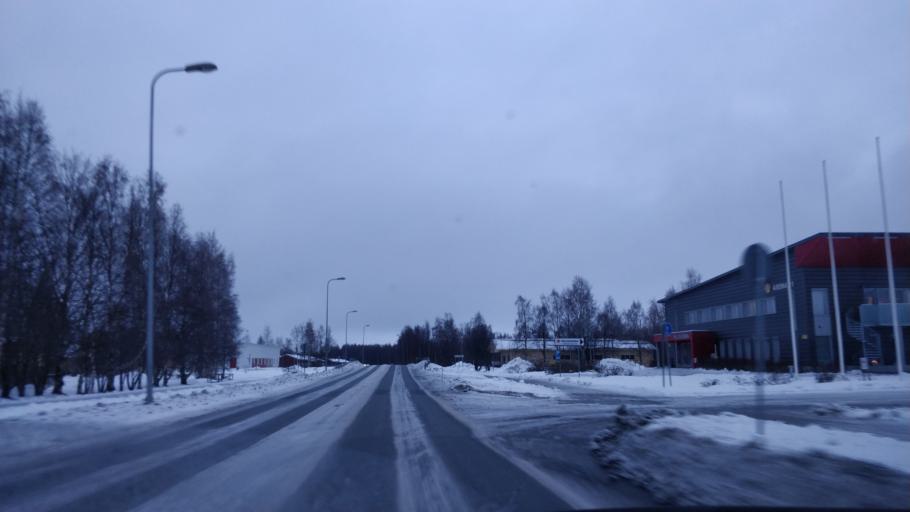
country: FI
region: Lapland
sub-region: Kemi-Tornio
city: Kemi
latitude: 65.7432
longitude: 24.5898
